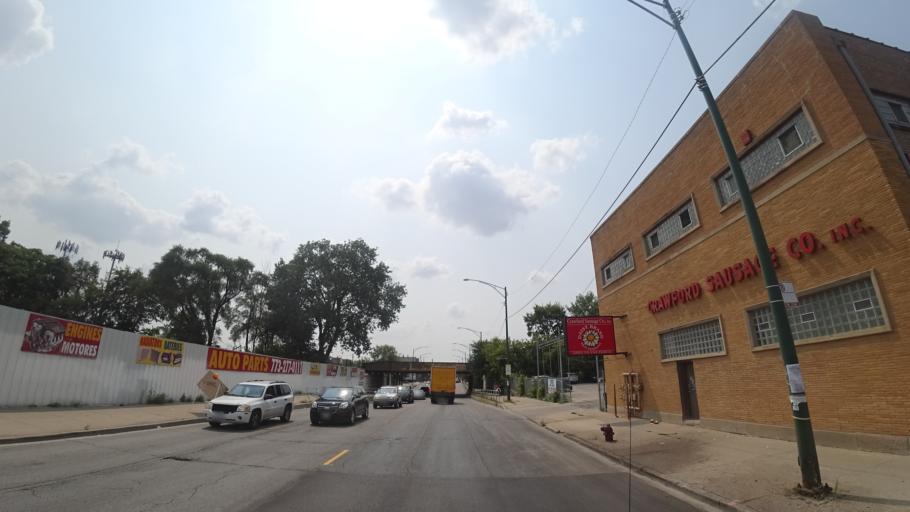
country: US
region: Illinois
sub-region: Cook County
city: Cicero
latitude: 41.8495
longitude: -87.7247
